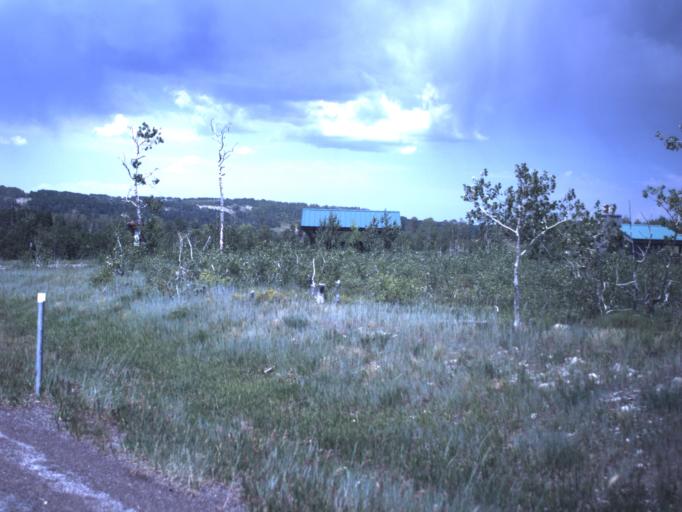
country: US
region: Utah
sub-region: Sanpete County
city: Fairview
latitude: 39.6776
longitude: -111.3125
